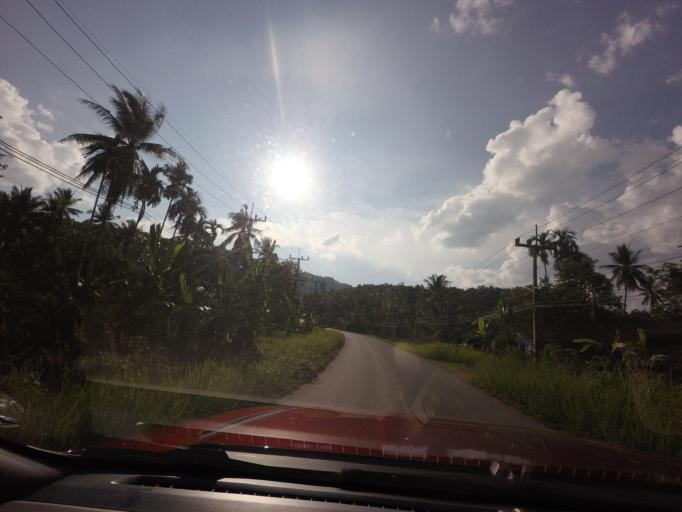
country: TH
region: Yala
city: Than To
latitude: 6.1977
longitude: 101.2410
